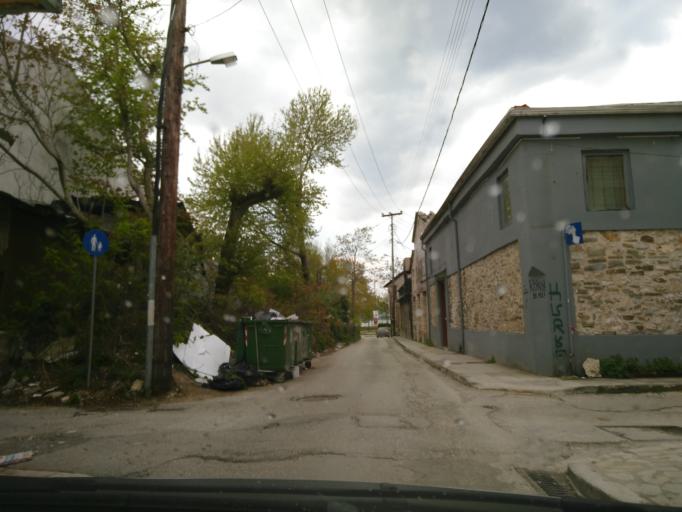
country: GR
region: Epirus
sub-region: Nomos Ioanninon
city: Ioannina
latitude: 39.6681
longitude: 20.8583
